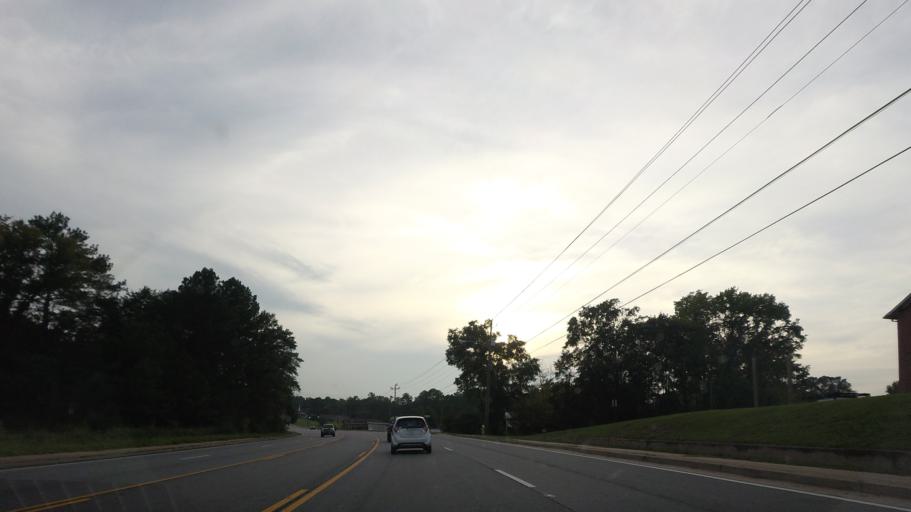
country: US
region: Georgia
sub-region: Bibb County
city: Macon
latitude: 32.8657
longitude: -83.5846
